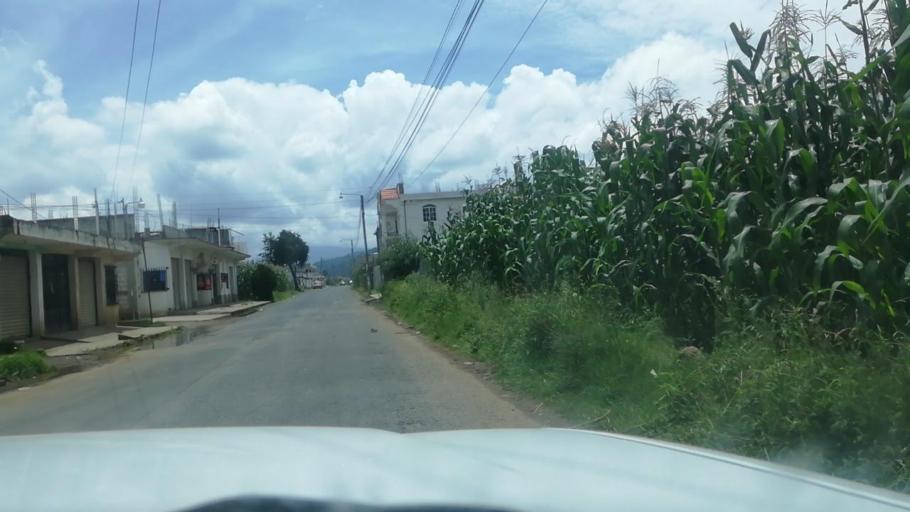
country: GT
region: Totonicapan
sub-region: Municipio de San Andres Xecul
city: San Andres Xecul
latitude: 14.9052
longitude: -91.4691
